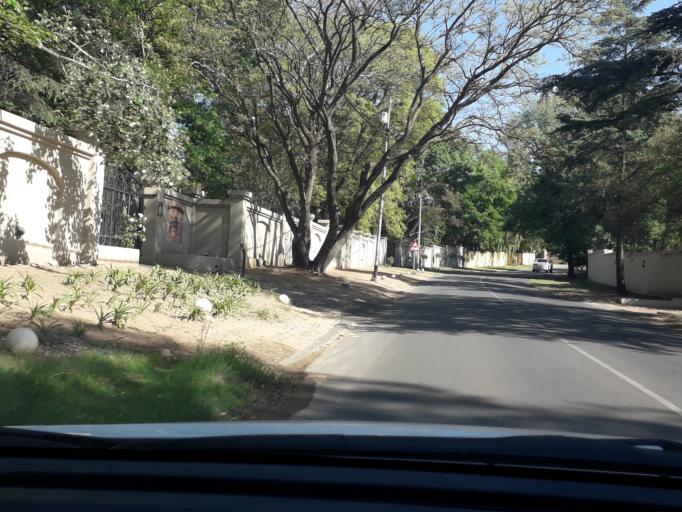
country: ZA
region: Gauteng
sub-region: City of Johannesburg Metropolitan Municipality
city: Midrand
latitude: -26.0701
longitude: 28.0337
